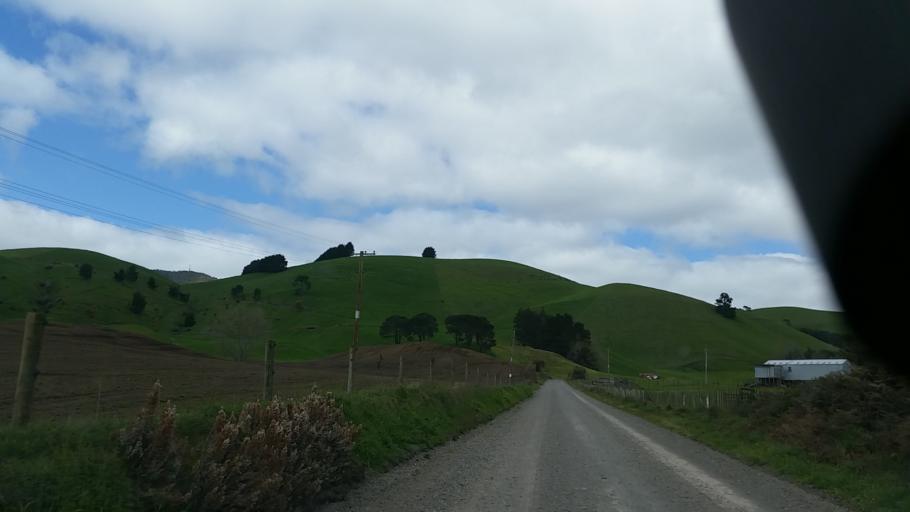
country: NZ
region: Bay of Plenty
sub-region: Rotorua District
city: Rotorua
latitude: -38.3534
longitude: 176.2317
